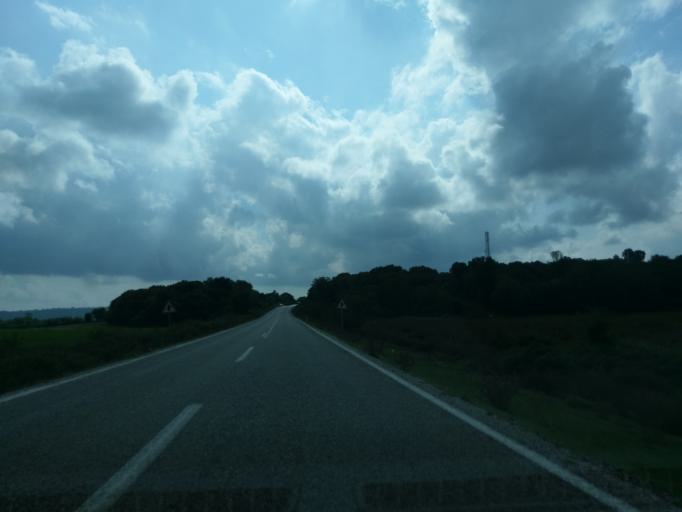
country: TR
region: Sinop
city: Sinop
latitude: 42.0241
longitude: 35.0436
